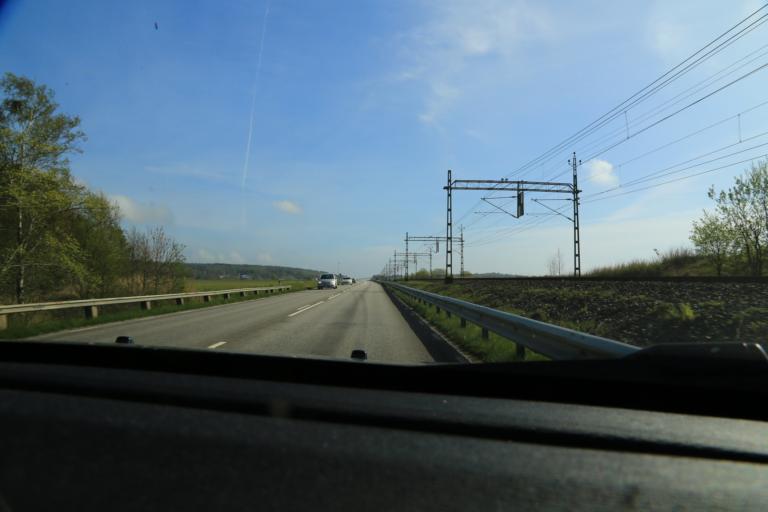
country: SE
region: Halland
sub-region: Varbergs Kommun
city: Varberg
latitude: 57.2090
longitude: 12.2217
